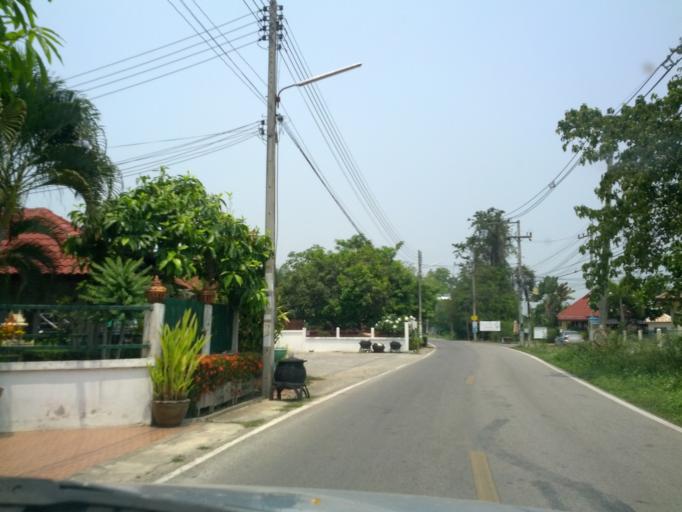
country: TH
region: Chiang Mai
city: San Sai
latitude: 18.8693
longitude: 99.0948
